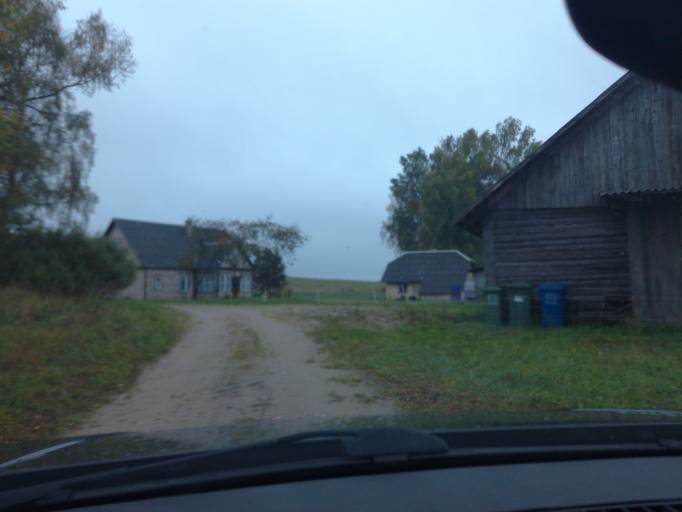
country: LT
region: Alytaus apskritis
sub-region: Alytus
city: Alytus
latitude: 54.4049
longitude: 24.1025
